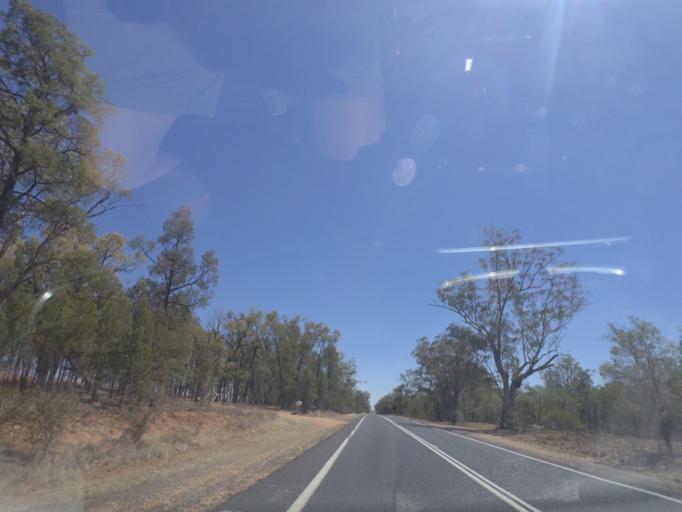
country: AU
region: New South Wales
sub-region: Gilgandra
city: Gilgandra
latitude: -31.4810
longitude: 148.8874
